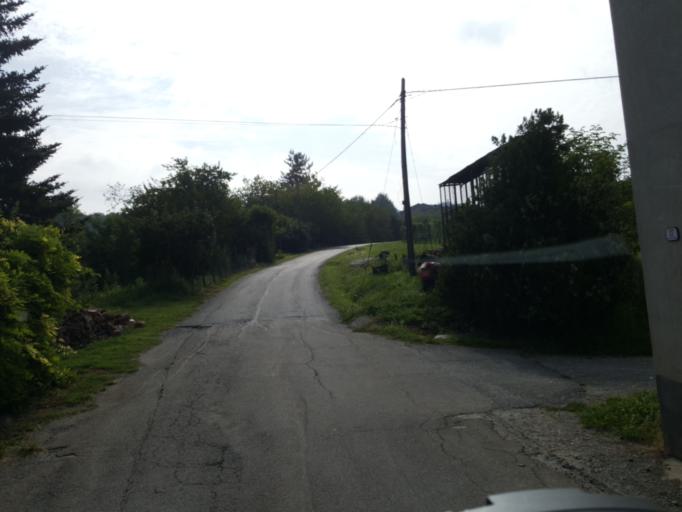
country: IT
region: Piedmont
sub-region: Provincia di Cuneo
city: Novello
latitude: 44.5949
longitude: 7.9120
